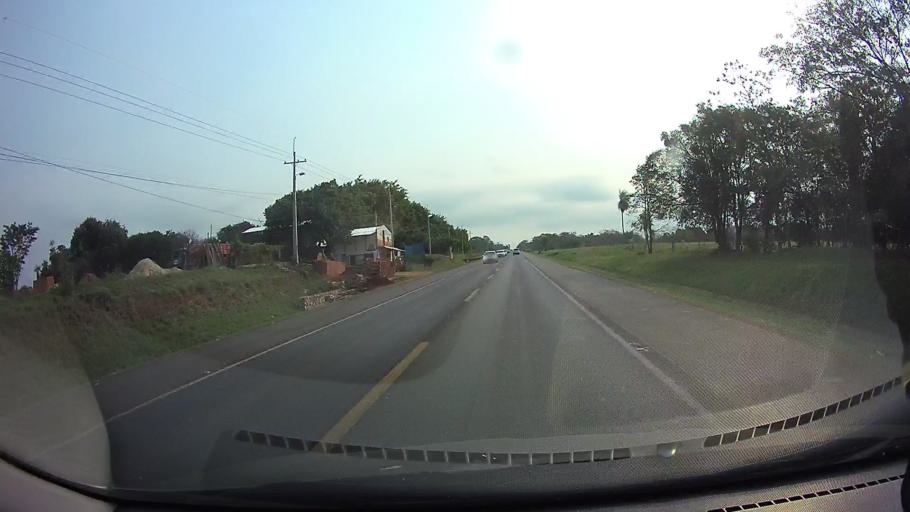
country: PY
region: Cordillera
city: Arroyos y Esteros
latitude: -25.0542
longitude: -57.1145
